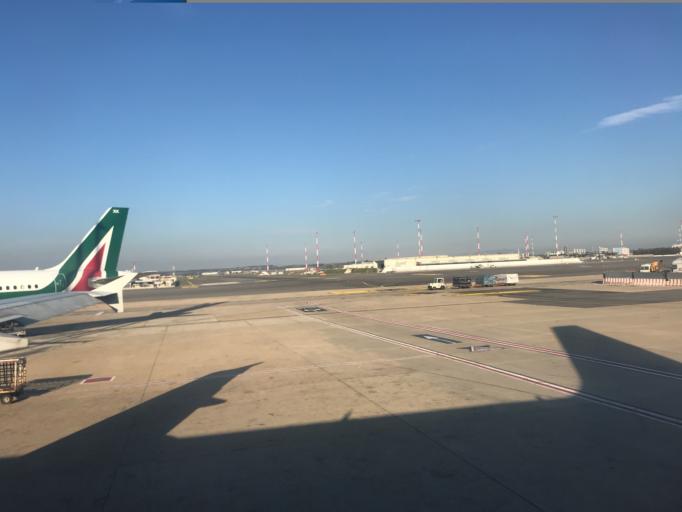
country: IT
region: Latium
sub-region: Citta metropolitana di Roma Capitale
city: Fiumicino-Isola Sacra
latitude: 41.7975
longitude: 12.2567
